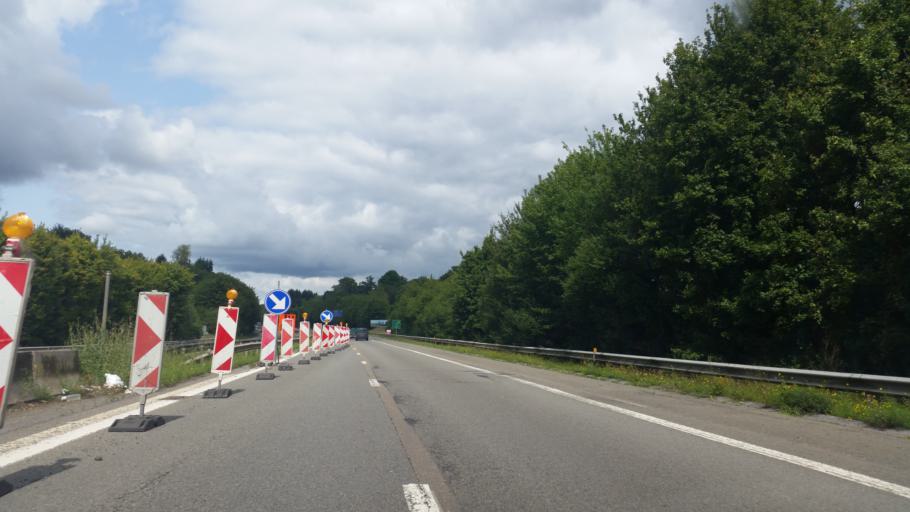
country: BE
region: Wallonia
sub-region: Province de Namur
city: Houyet
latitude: 50.2111
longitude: 5.0655
